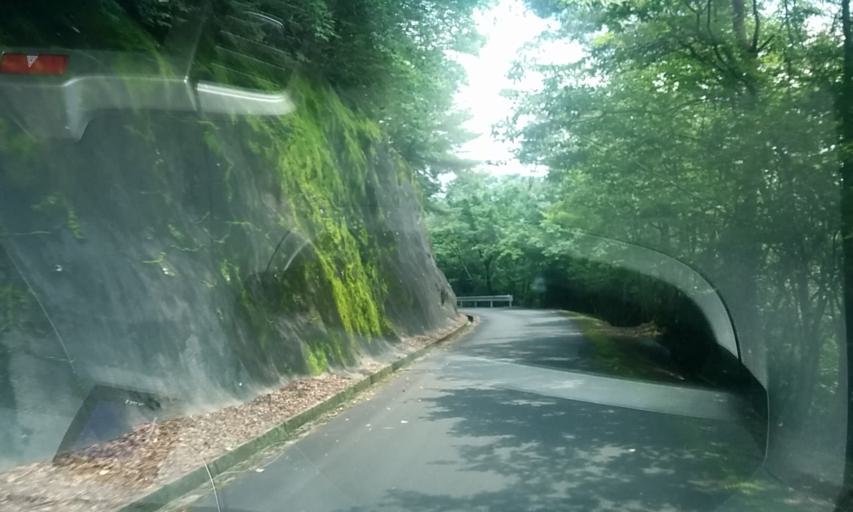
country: JP
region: Hyogo
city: Sasayama
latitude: 35.1685
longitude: 135.2028
